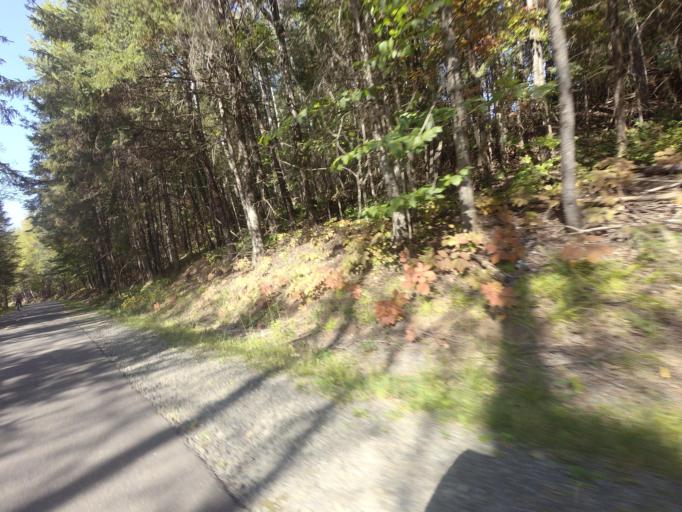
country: CA
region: Quebec
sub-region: Laurentides
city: Mont-Tremblant
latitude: 46.1280
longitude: -74.5739
